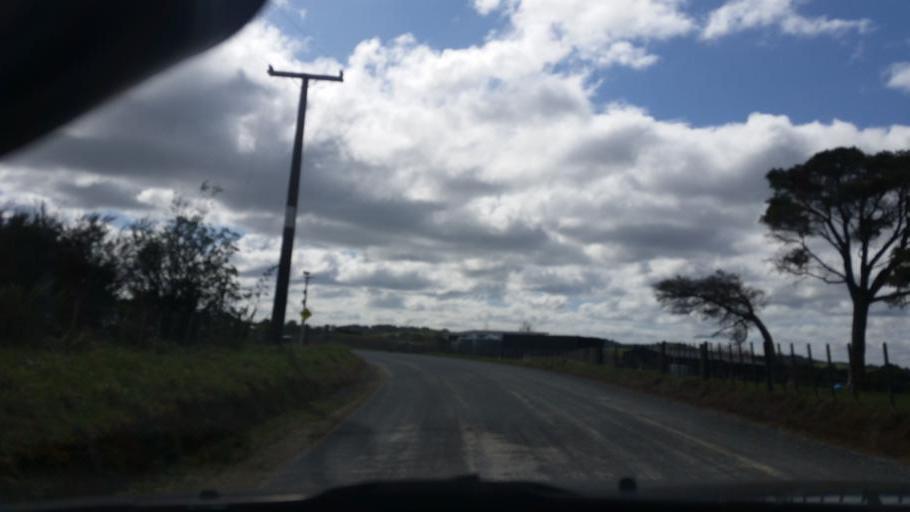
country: NZ
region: Auckland
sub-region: Auckland
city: Wellsford
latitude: -36.1454
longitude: 174.5076
